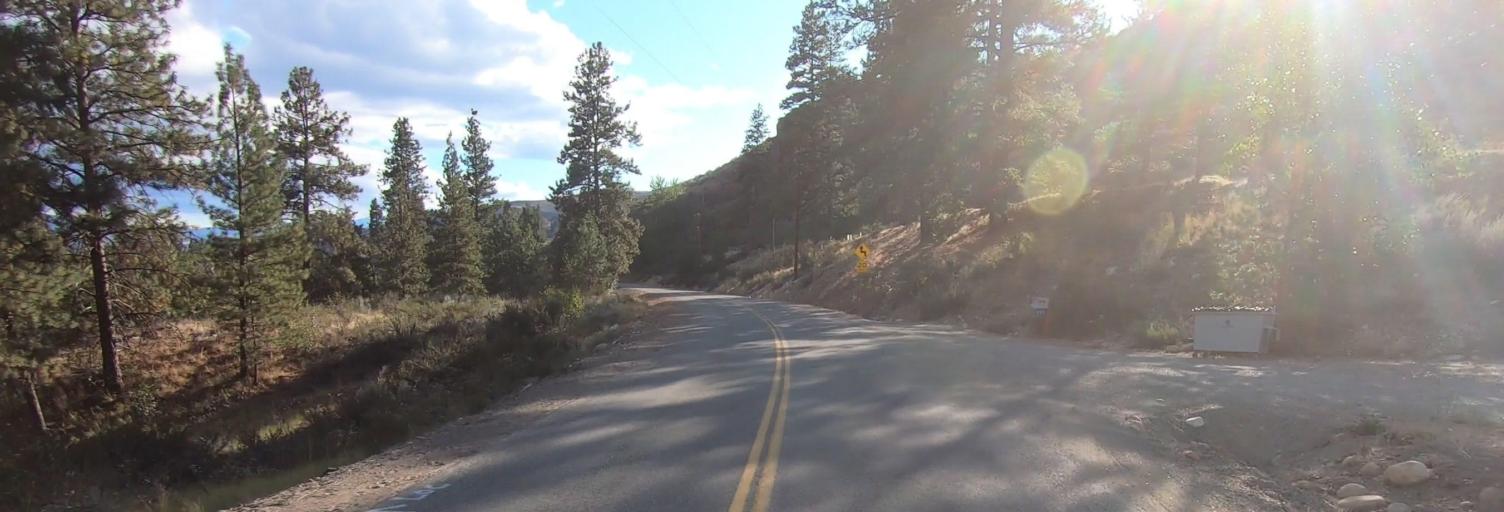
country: US
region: Washington
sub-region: Okanogan County
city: Brewster
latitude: 48.5562
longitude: -120.1848
